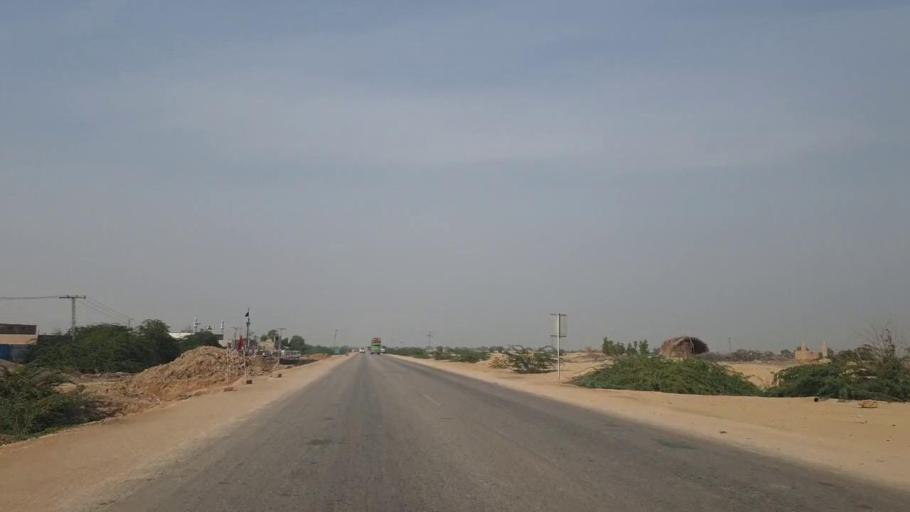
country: PK
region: Sindh
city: Sann
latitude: 26.0602
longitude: 68.1039
